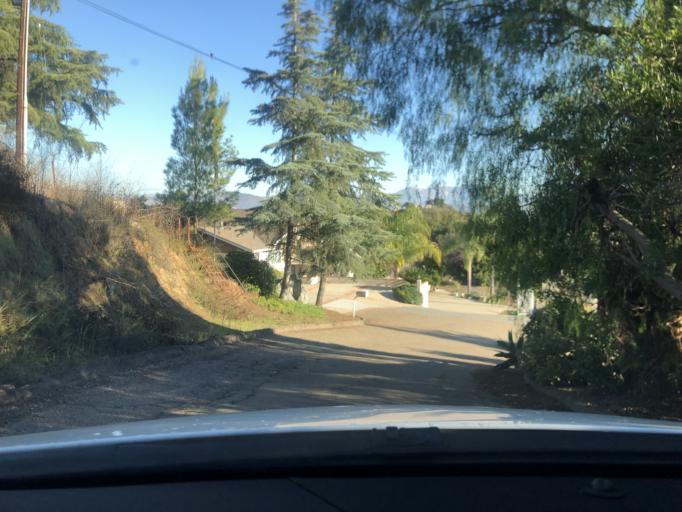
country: US
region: California
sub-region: San Diego County
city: Casa de Oro-Mount Helix
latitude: 32.7756
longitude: -116.9599
